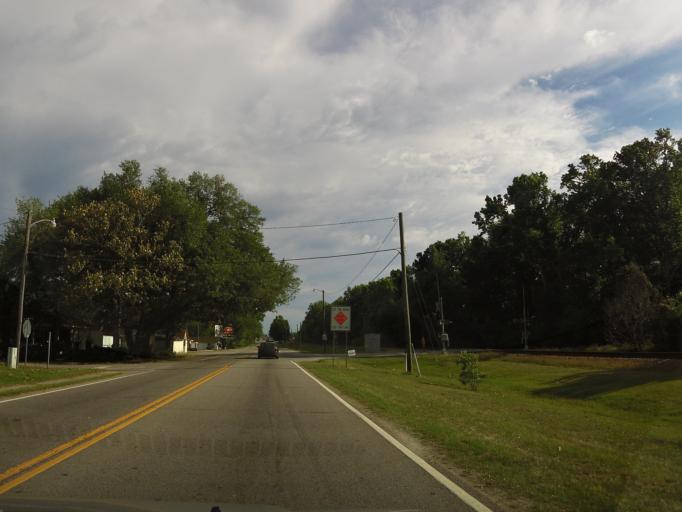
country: US
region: South Carolina
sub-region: Hampton County
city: Estill
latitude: 32.7643
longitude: -81.2411
